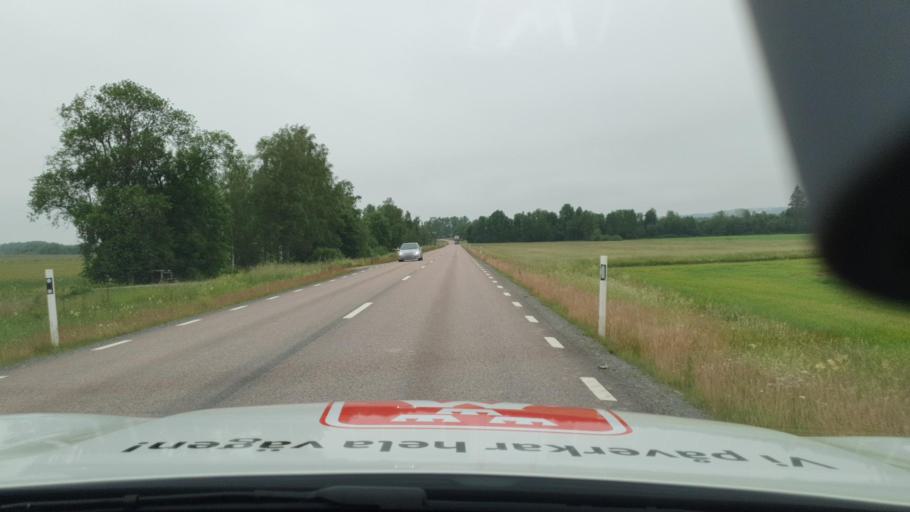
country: SE
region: Vaermland
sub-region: Sunne Kommun
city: Sunne
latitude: 59.6557
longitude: 13.1537
